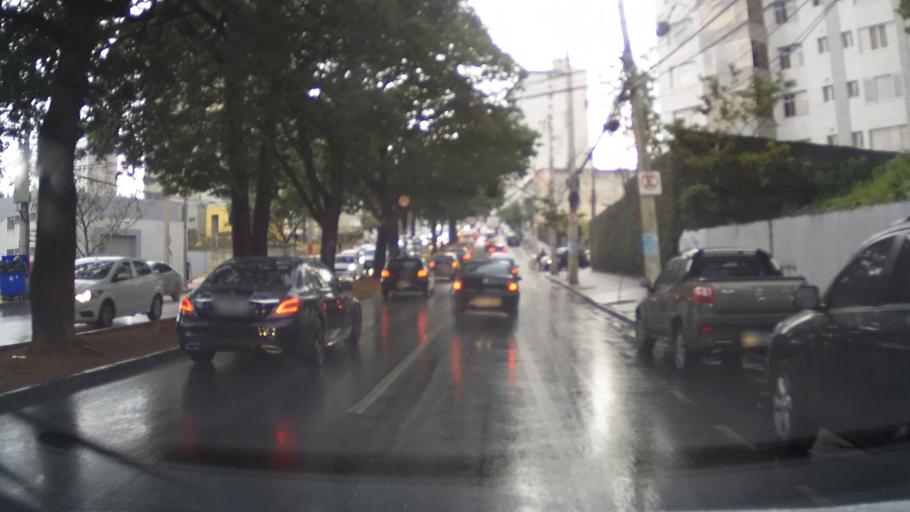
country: BR
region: Minas Gerais
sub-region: Belo Horizonte
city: Belo Horizonte
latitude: -19.9453
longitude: -43.9573
